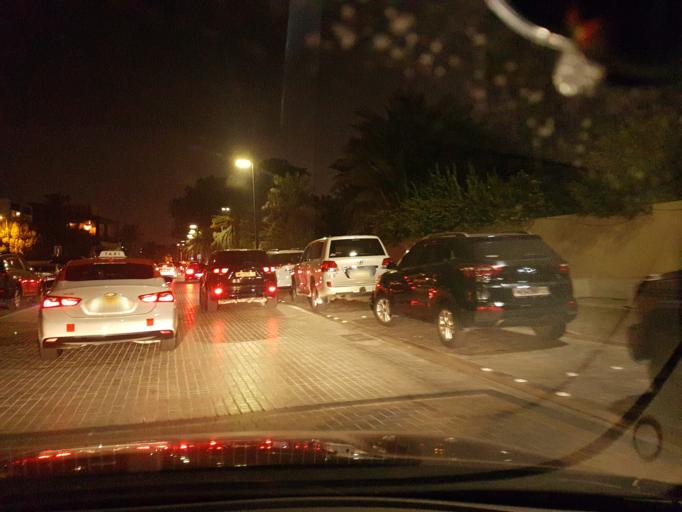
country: BH
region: Manama
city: Manama
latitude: 26.2145
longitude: 50.5930
